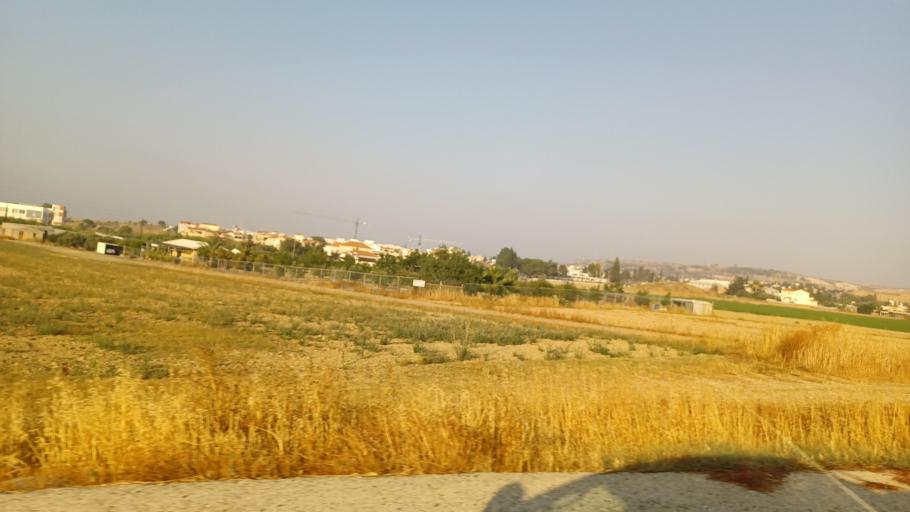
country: CY
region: Larnaka
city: Pyla
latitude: 35.0119
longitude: 33.6978
